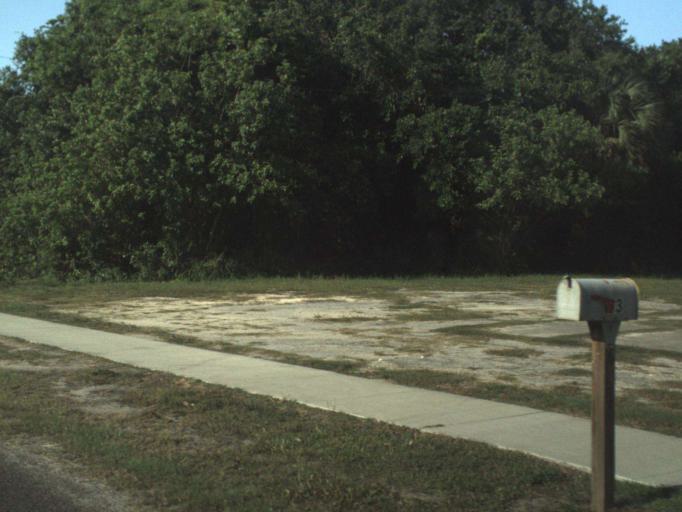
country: US
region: Florida
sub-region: Volusia County
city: Oak Hill
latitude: 28.8621
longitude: -80.8513
